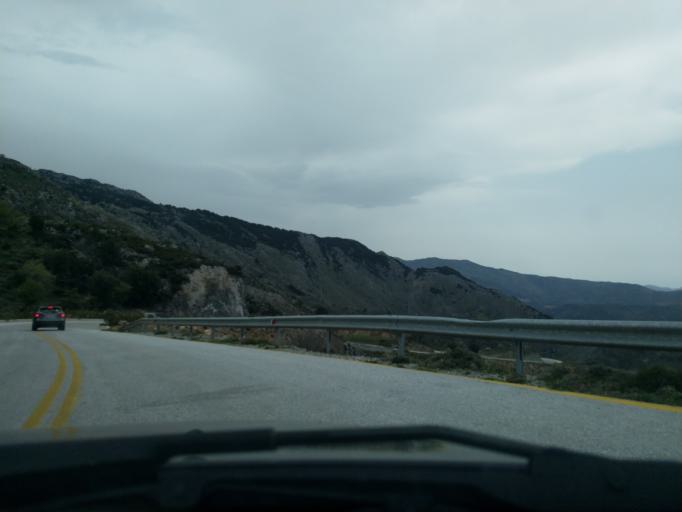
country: GR
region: Crete
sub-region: Nomos Chanias
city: Gerani
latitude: 35.3718
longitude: 23.9017
